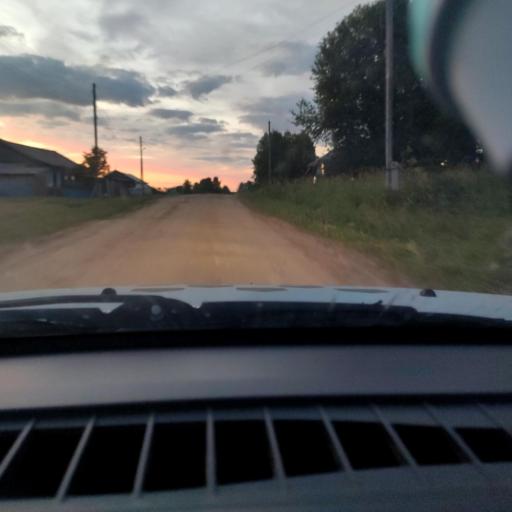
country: RU
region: Kirov
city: Darovskoy
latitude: 58.9900
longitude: 47.8674
